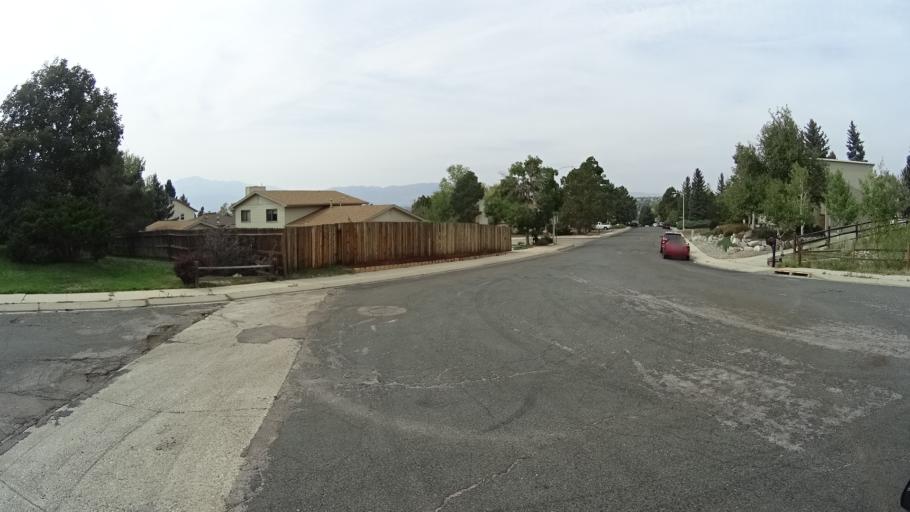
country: US
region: Colorado
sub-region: El Paso County
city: Cimarron Hills
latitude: 38.8980
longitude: -104.7290
